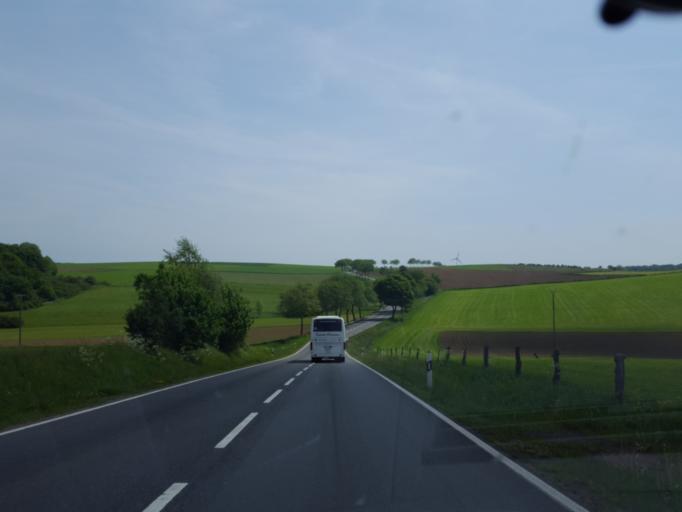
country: DE
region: North Rhine-Westphalia
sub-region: Regierungsbezirk Arnsberg
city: Brilon
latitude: 51.4124
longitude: 8.6649
